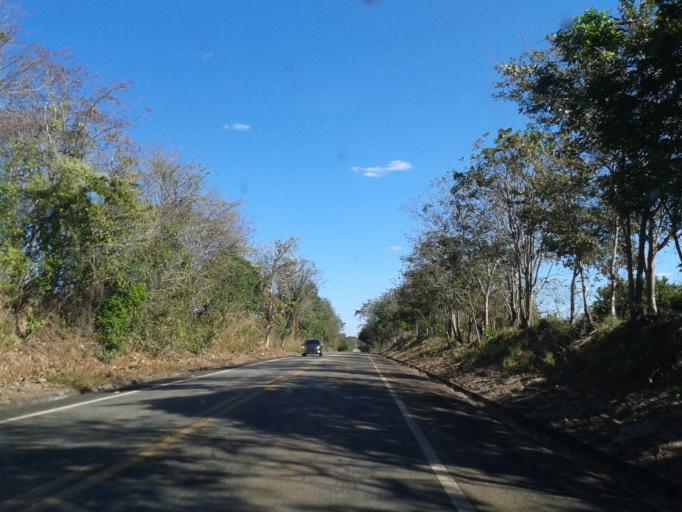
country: BR
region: Goias
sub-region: Mozarlandia
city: Mozarlandia
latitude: -14.5679
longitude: -50.4998
